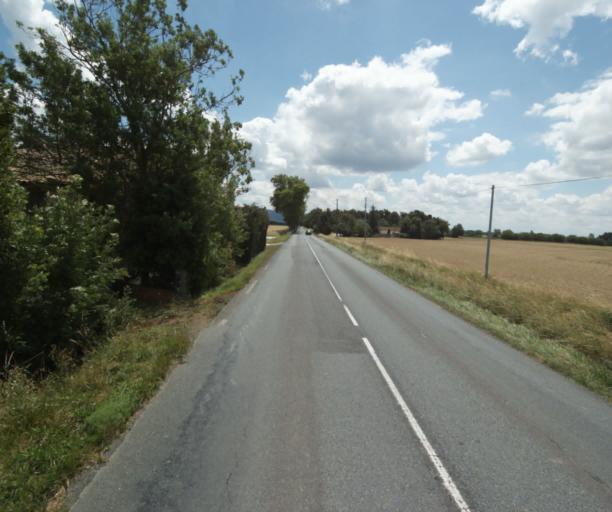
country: FR
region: Midi-Pyrenees
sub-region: Departement de la Haute-Garonne
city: Revel
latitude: 43.5019
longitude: 2.0118
